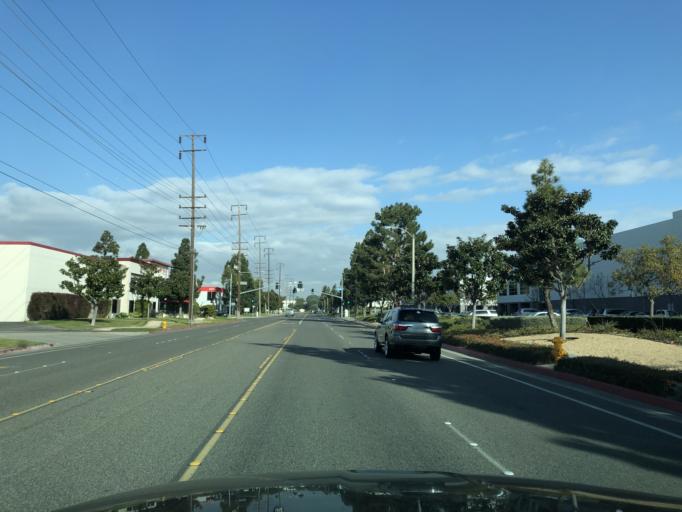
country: US
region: California
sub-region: Orange County
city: Westminster
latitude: 33.7398
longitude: -118.0328
